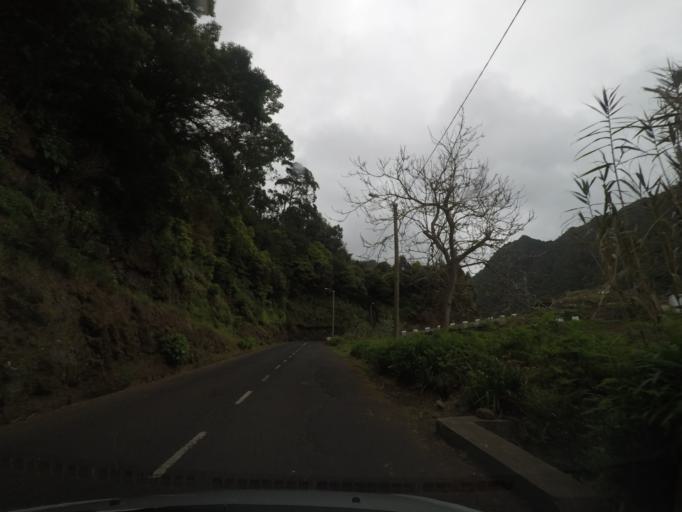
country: PT
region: Madeira
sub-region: Santana
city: Santana
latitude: 32.7521
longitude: -16.8385
